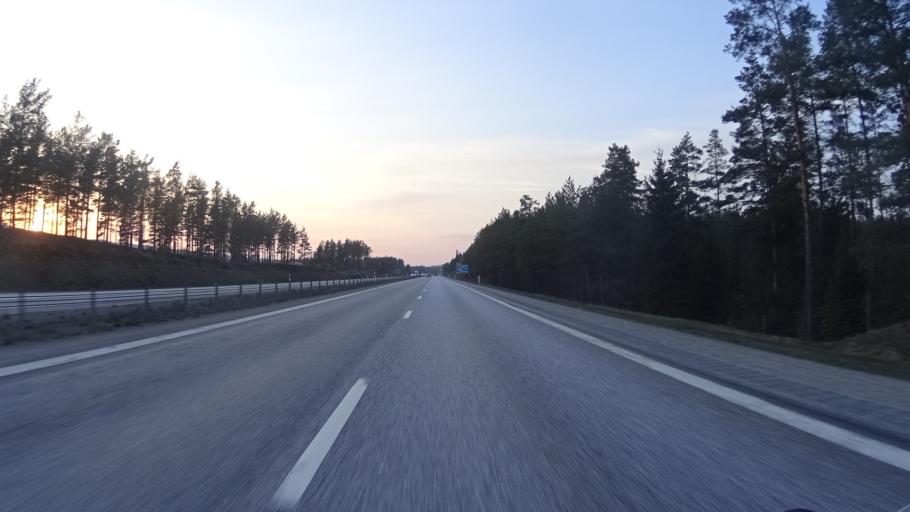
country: SE
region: Joenkoeping
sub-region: Jonkopings Kommun
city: Odensjo
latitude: 57.6756
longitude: 14.1704
